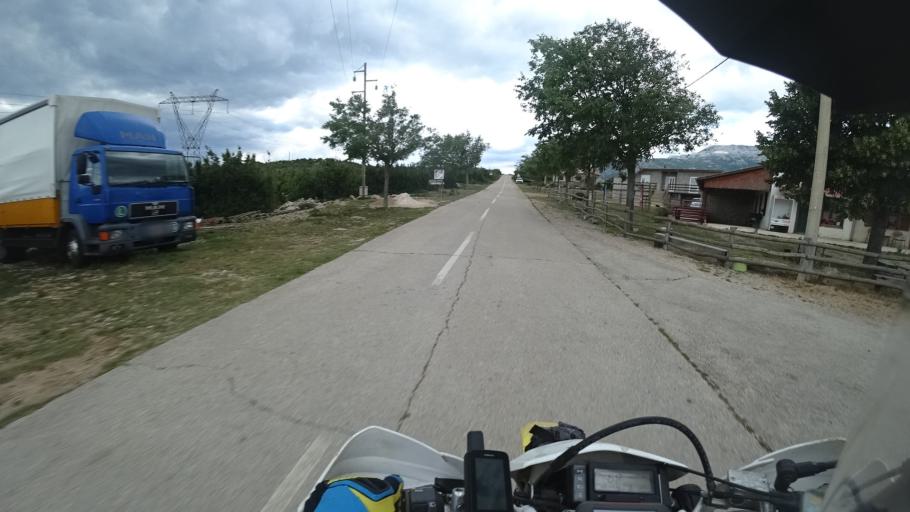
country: HR
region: Zadarska
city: Gracac
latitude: 44.2029
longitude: 15.8587
